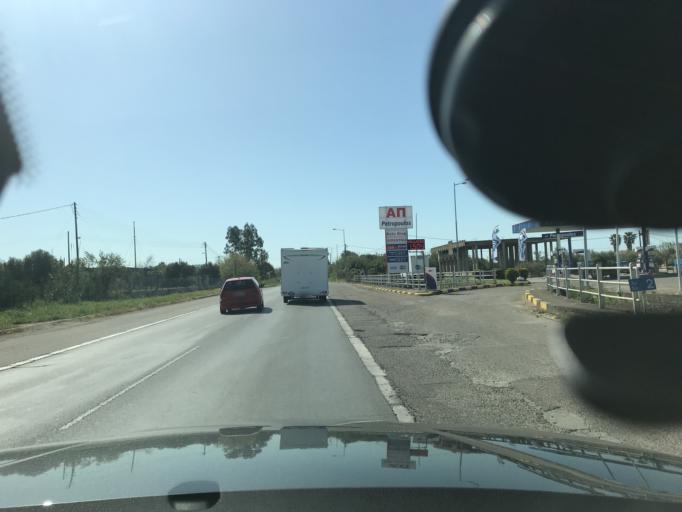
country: GR
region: West Greece
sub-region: Nomos Ileias
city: Pyrgos
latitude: 37.6597
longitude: 21.4628
